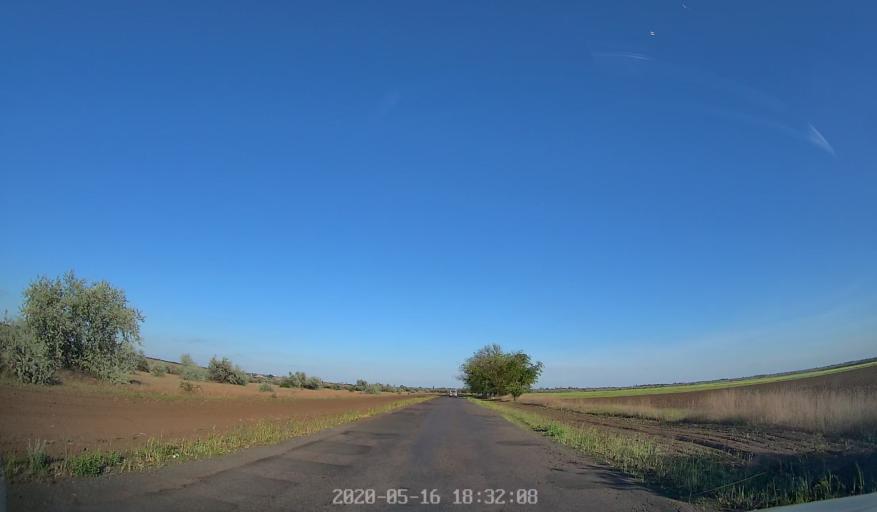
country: UA
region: Odessa
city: Lymanske
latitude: 46.5393
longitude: 30.0498
